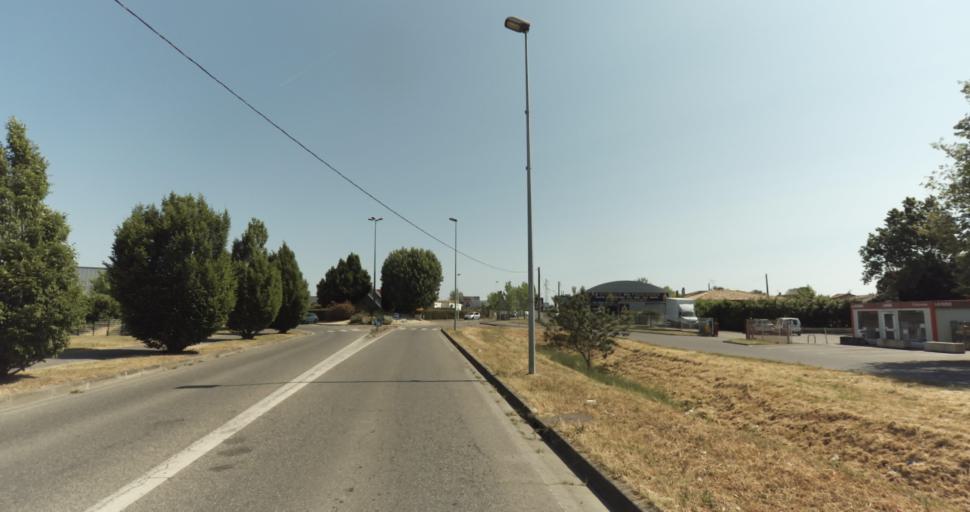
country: FR
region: Midi-Pyrenees
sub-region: Departement de la Haute-Garonne
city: La Salvetat-Saint-Gilles
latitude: 43.5816
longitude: 1.2739
